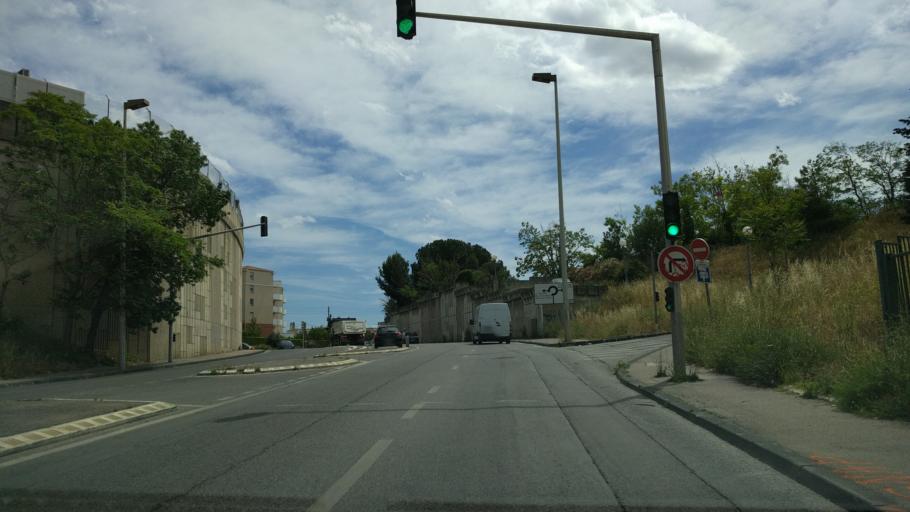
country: FR
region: Provence-Alpes-Cote d'Azur
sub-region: Departement des Bouches-du-Rhone
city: Marseille 13
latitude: 43.3294
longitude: 5.3978
